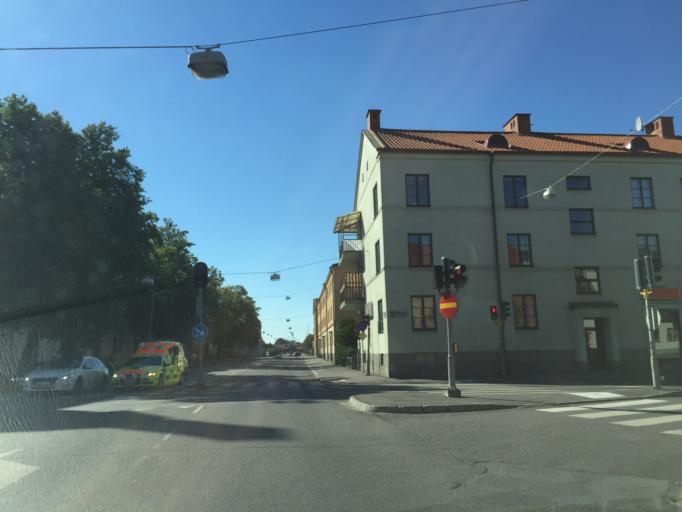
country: SE
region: OErebro
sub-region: Orebro Kommun
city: Orebro
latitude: 59.2744
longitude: 15.2010
